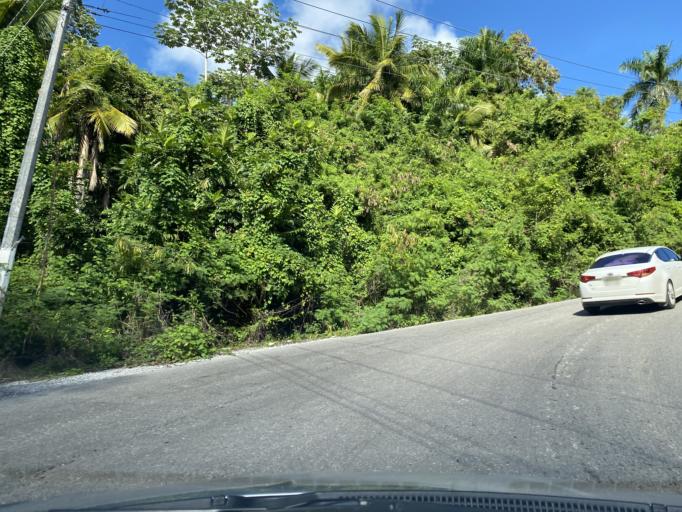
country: DO
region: Samana
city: Sanchez
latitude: 19.2348
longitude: -69.5984
